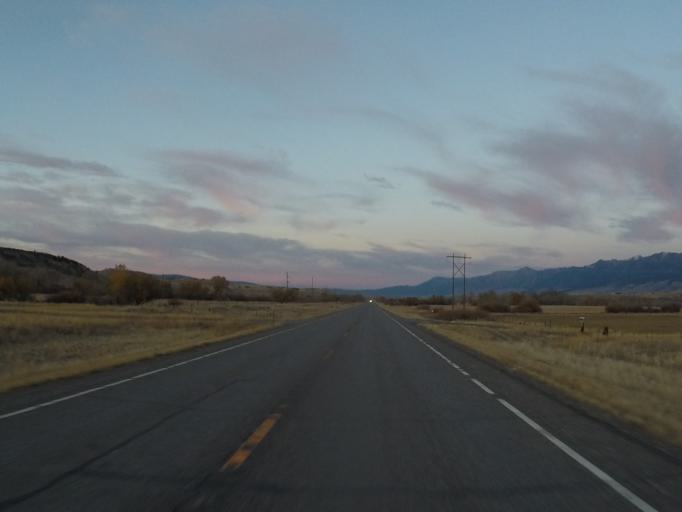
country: US
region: Montana
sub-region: Park County
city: Livingston
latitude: 45.3551
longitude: -110.7468
